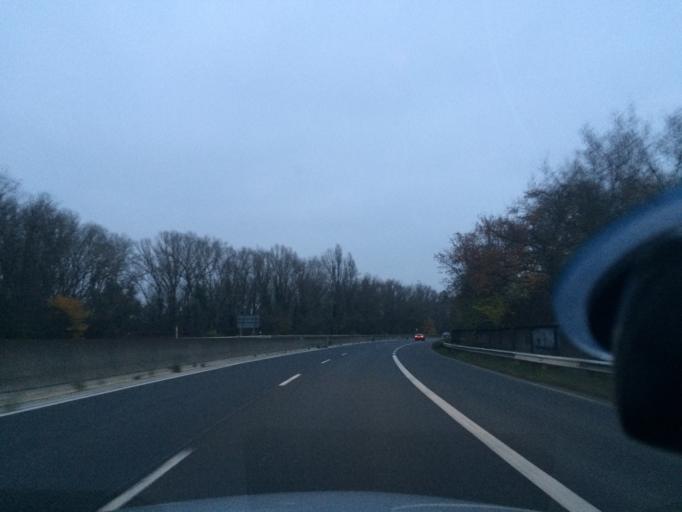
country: DE
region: Hesse
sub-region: Regierungsbezirk Darmstadt
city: Ginsheim-Gustavsburg
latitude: 49.9666
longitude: 8.3225
